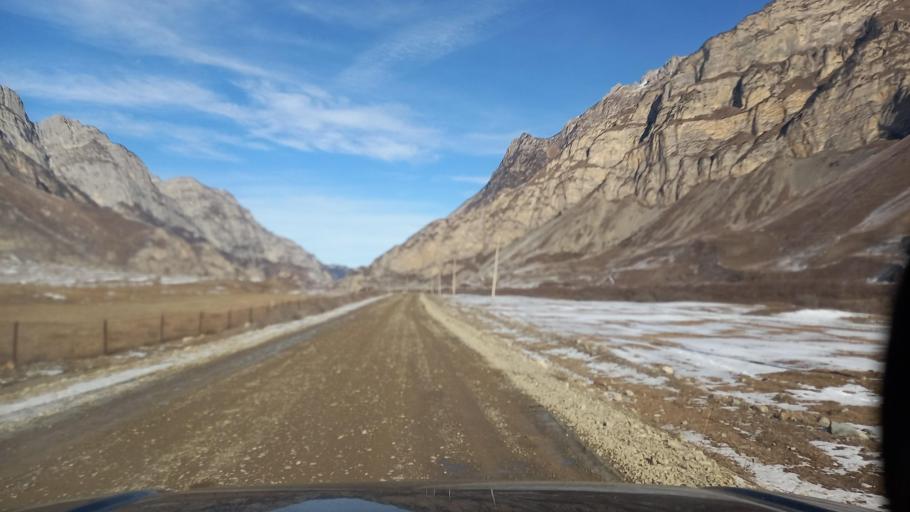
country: RU
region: North Ossetia
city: Verkhniy Fiagdon
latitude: 42.8457
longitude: 44.4438
